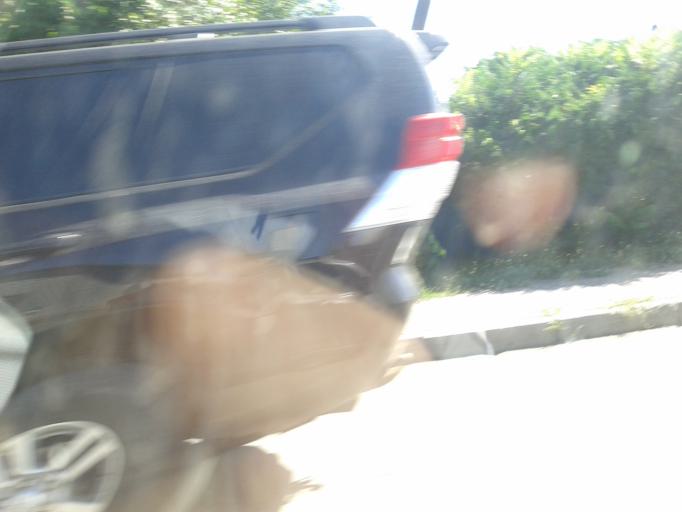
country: RU
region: Volgograd
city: Volgograd
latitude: 48.7038
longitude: 44.4495
